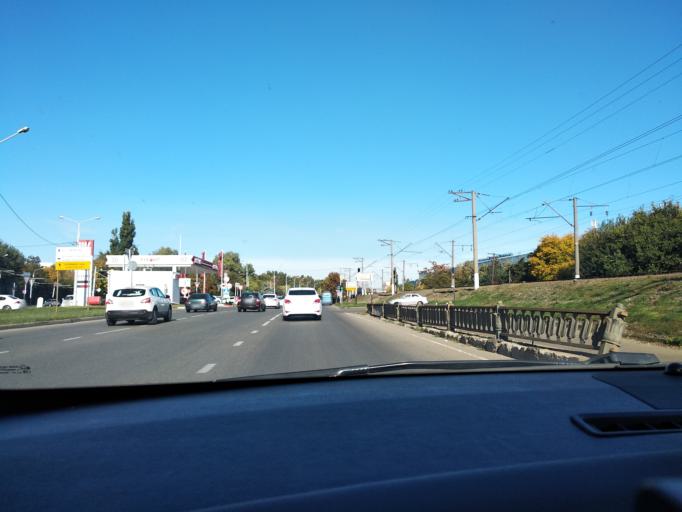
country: RU
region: Adygeya
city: Yablonovskiy
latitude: 45.0067
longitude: 38.9678
